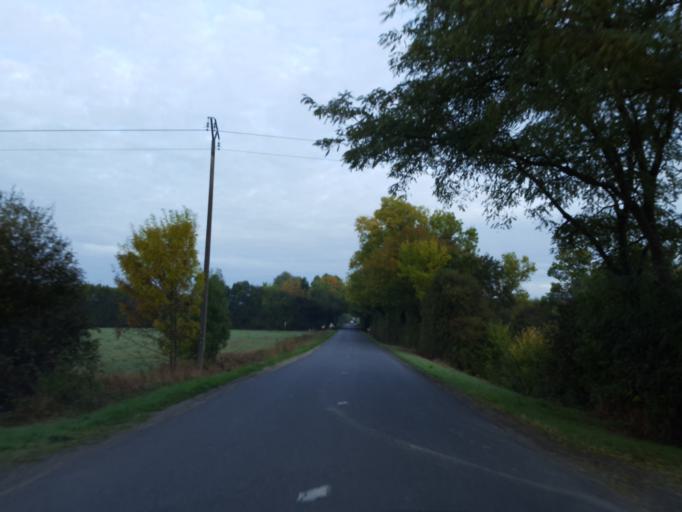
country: FR
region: Pays de la Loire
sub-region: Departement de la Loire-Atlantique
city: Saint-Julien-de-Concelles
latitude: 47.2508
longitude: -1.4054
